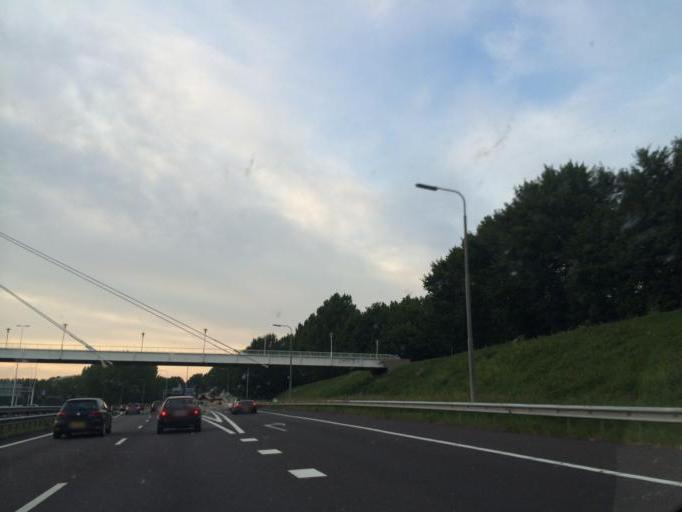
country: NL
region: South Holland
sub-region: Gemeente Capelle aan den IJssel
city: Capelle-West
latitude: 51.8900
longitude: 4.5624
